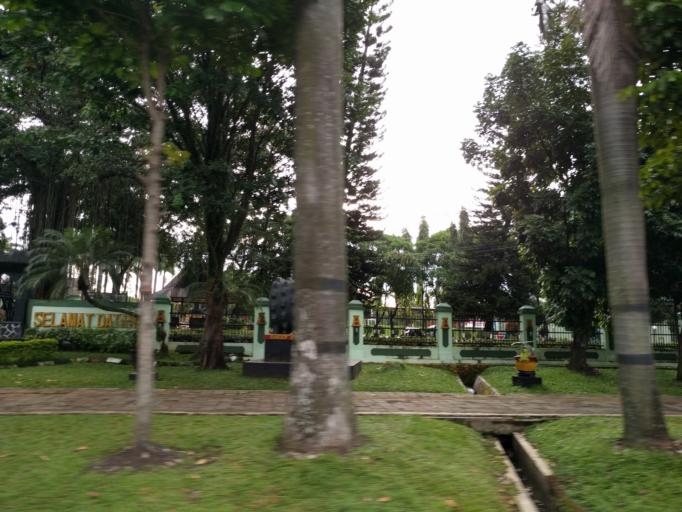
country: ID
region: West Java
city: Bogor
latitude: -6.5835
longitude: 106.7968
